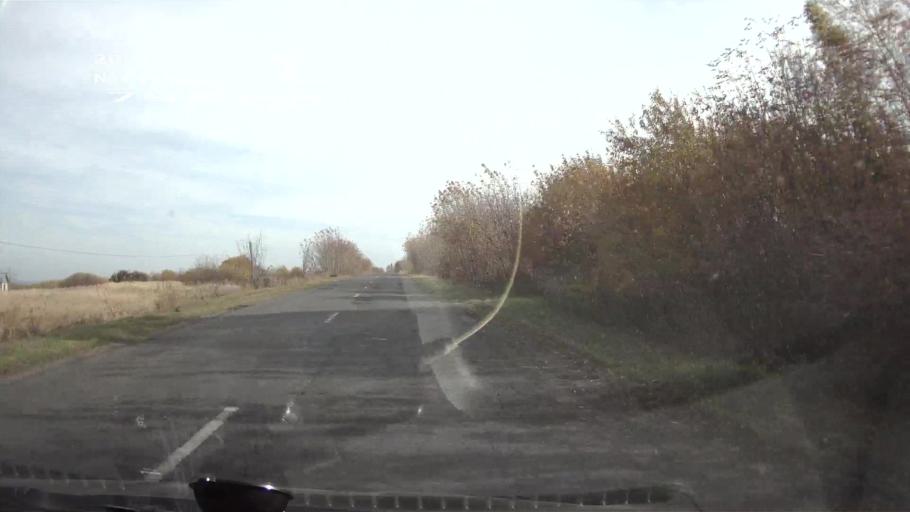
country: RU
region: Chuvashia
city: Alatyr'
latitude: 54.8448
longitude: 46.4629
